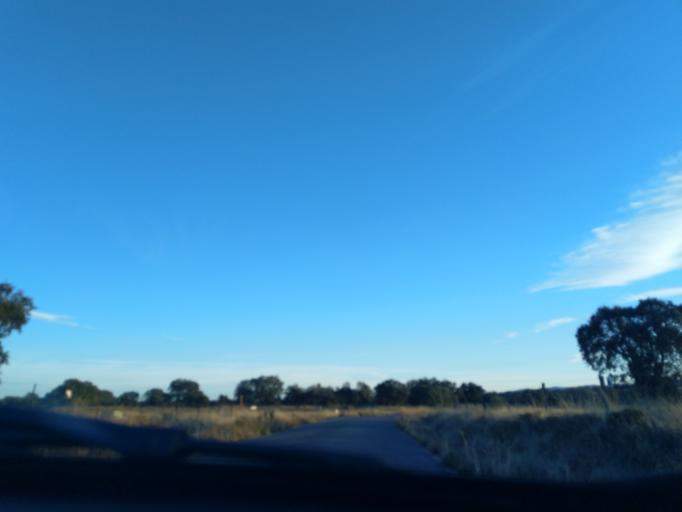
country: ES
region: Extremadura
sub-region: Provincia de Badajoz
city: Valverde de Llerena
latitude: 38.2433
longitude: -5.8246
